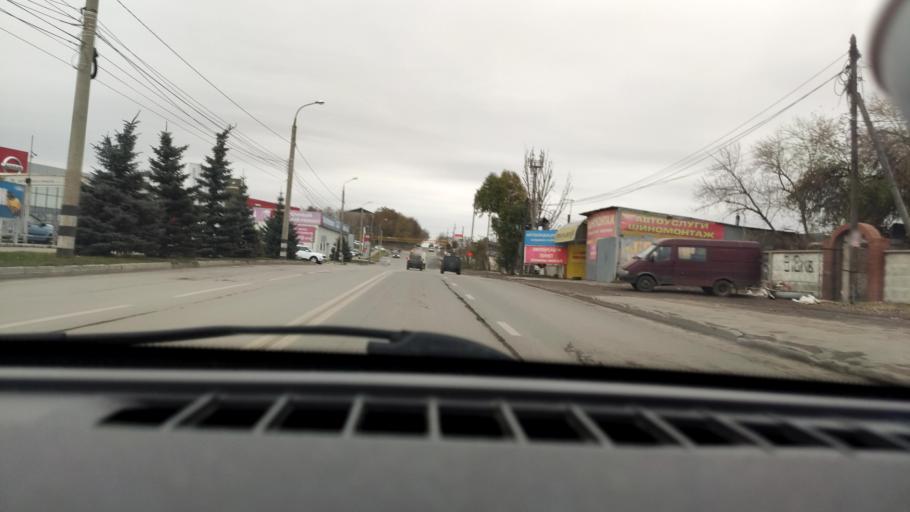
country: RU
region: Samara
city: Samara
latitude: 53.1841
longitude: 50.1502
